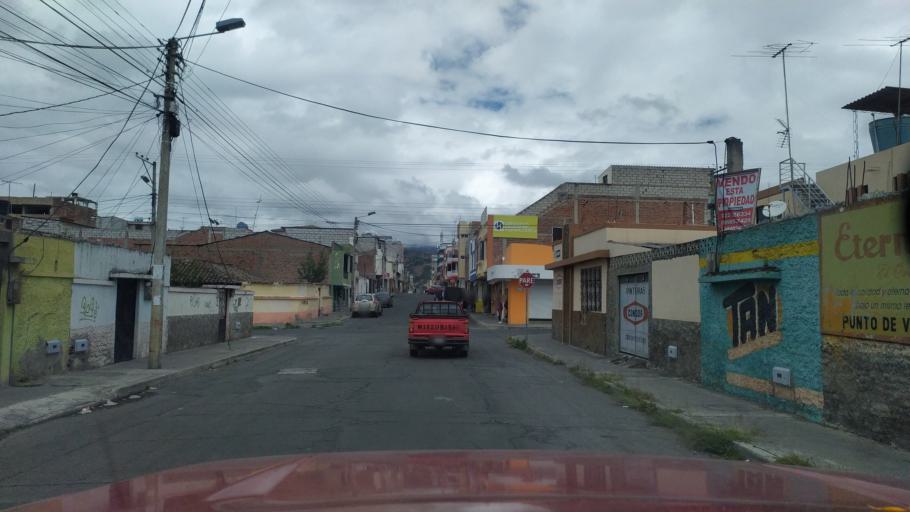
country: EC
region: Chimborazo
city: Riobamba
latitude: -1.6694
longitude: -78.6432
